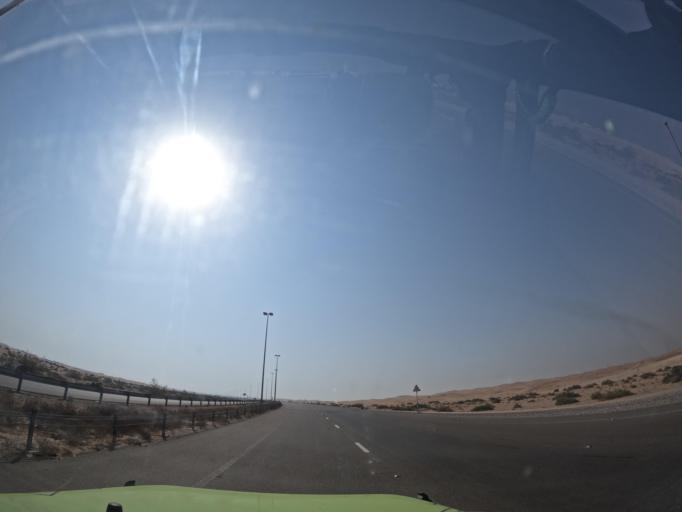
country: OM
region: Al Buraimi
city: Al Buraymi
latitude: 24.5196
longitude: 55.5550
